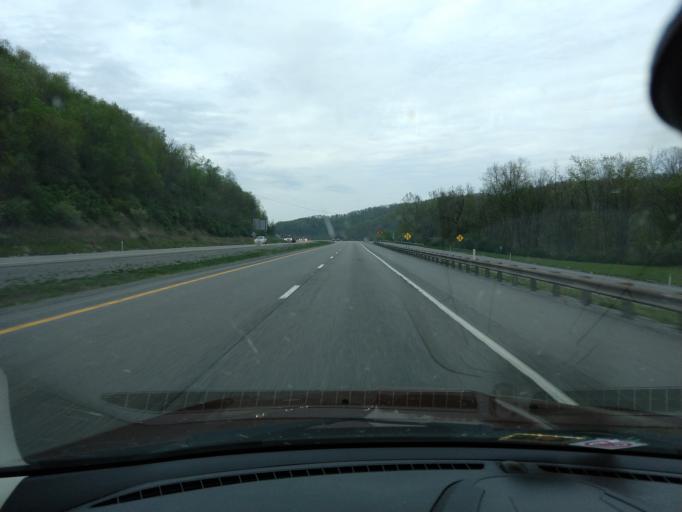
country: US
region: West Virginia
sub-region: Lewis County
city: Weston
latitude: 39.0235
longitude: -80.4261
